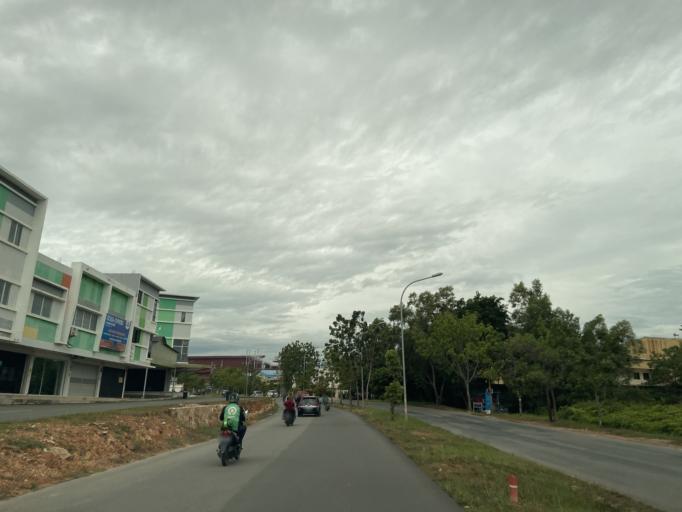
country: SG
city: Singapore
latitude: 1.1121
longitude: 104.0673
